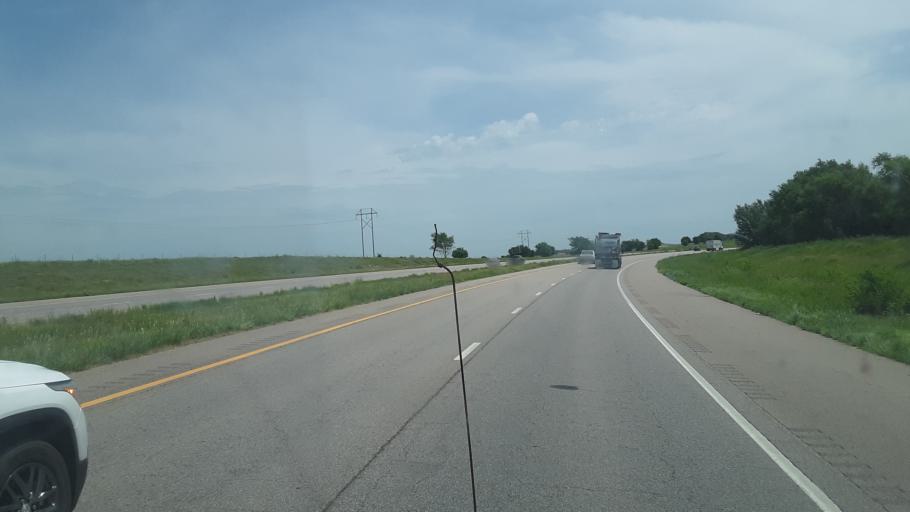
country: US
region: Kansas
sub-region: Butler County
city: Towanda
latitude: 37.8053
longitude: -96.9986
